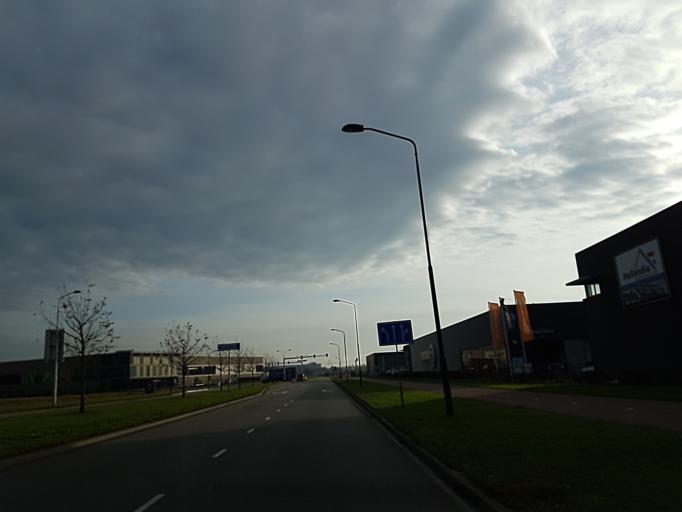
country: NL
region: North Brabant
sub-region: Roosendaal
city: Roosendaal
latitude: 51.5653
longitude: 4.4723
